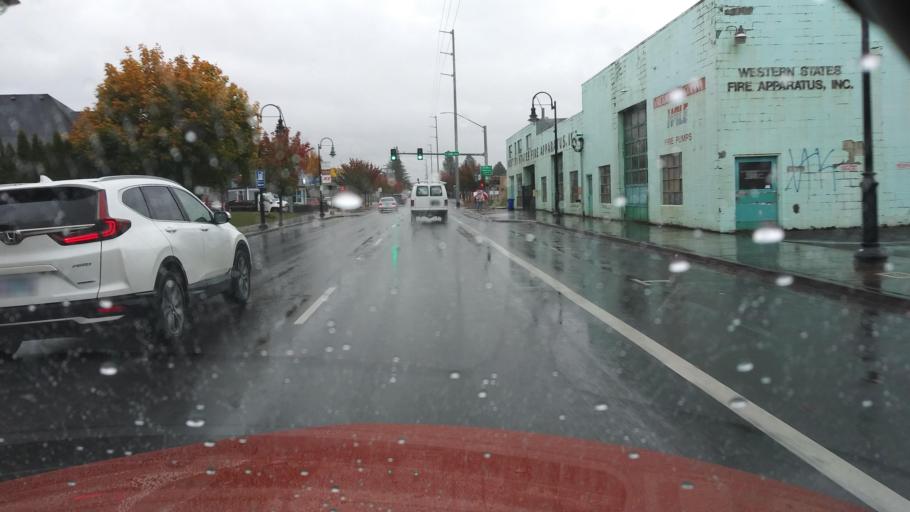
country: US
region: Oregon
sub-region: Washington County
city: Cornelius
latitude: 45.5201
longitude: -123.0557
